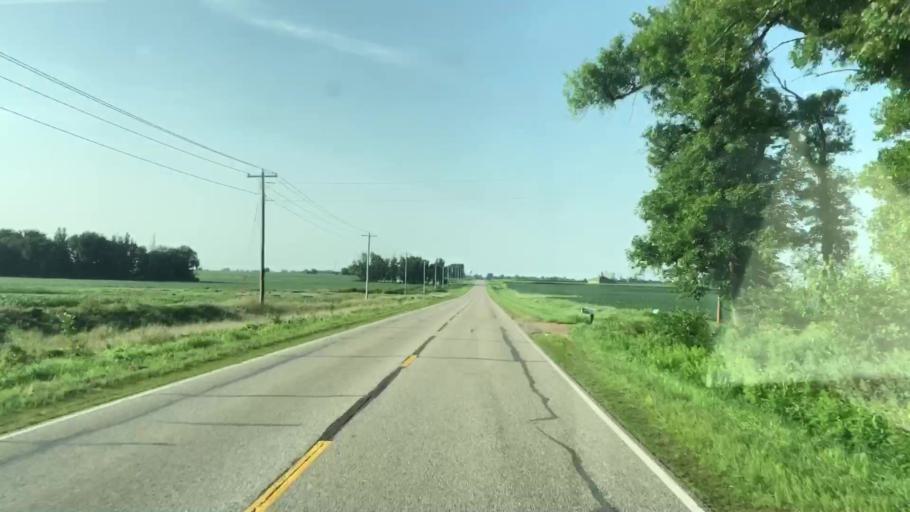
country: US
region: Iowa
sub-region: Lyon County
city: George
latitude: 43.3659
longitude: -95.9983
